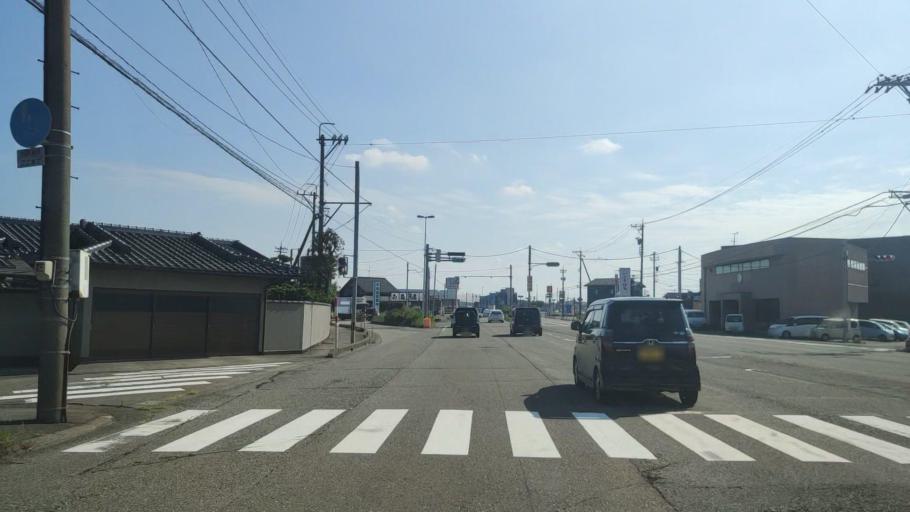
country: JP
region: Ishikawa
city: Matsuto
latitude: 36.5062
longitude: 136.5530
